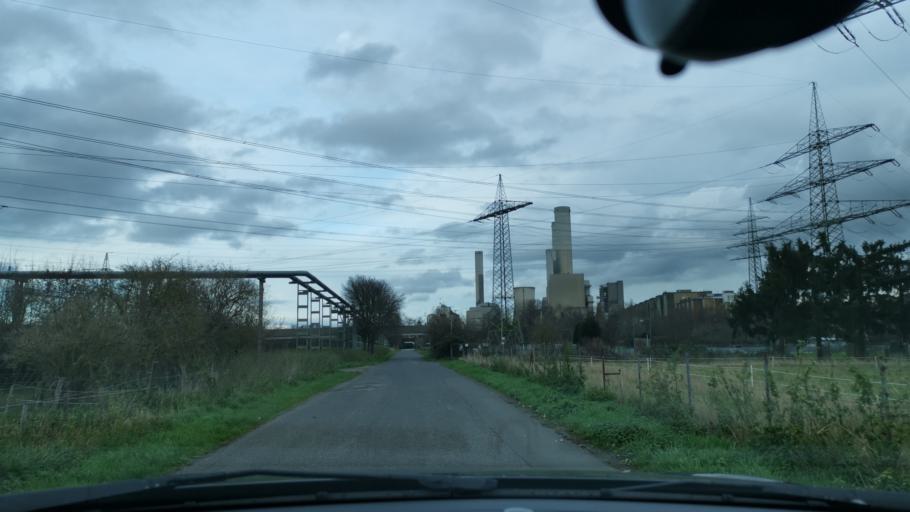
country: DE
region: North Rhine-Westphalia
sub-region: Regierungsbezirk Dusseldorf
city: Grevenbroich
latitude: 51.0478
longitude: 6.5716
